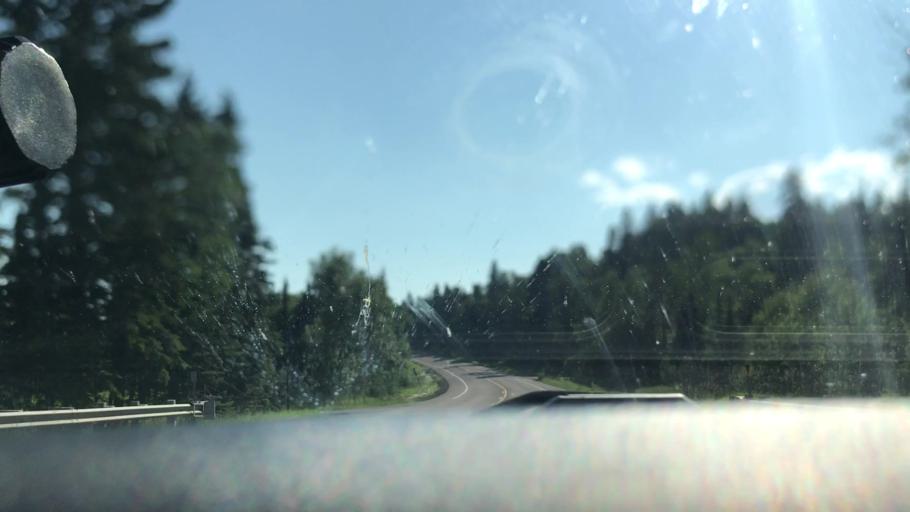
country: US
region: Minnesota
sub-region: Cook County
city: Grand Marais
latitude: 47.8178
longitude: -90.0521
